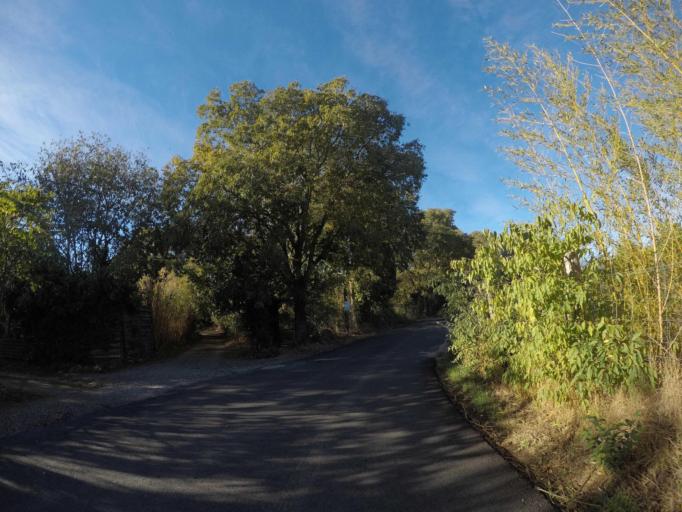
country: FR
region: Languedoc-Roussillon
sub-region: Departement des Pyrenees-Orientales
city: Llupia
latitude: 42.6057
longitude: 2.7722
